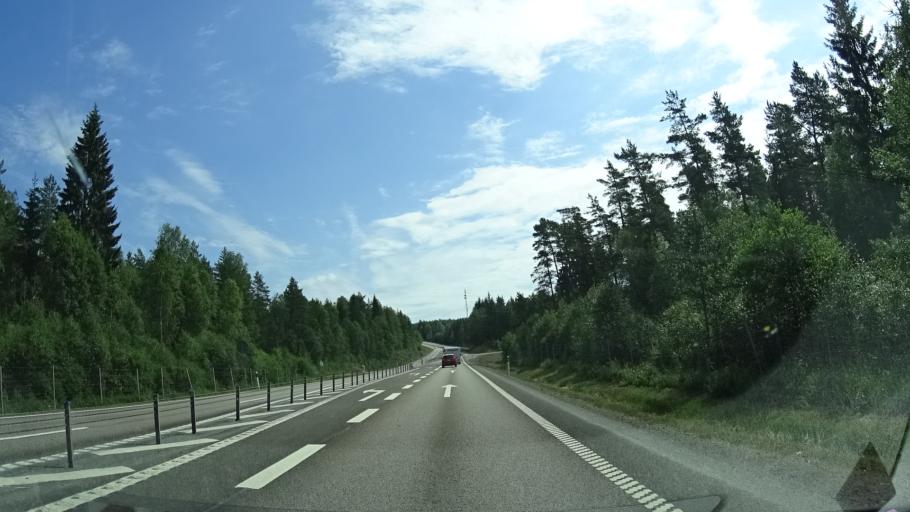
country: SE
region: Vaermland
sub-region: Kristinehamns Kommun
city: Bjorneborg
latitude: 59.3114
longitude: 14.2710
